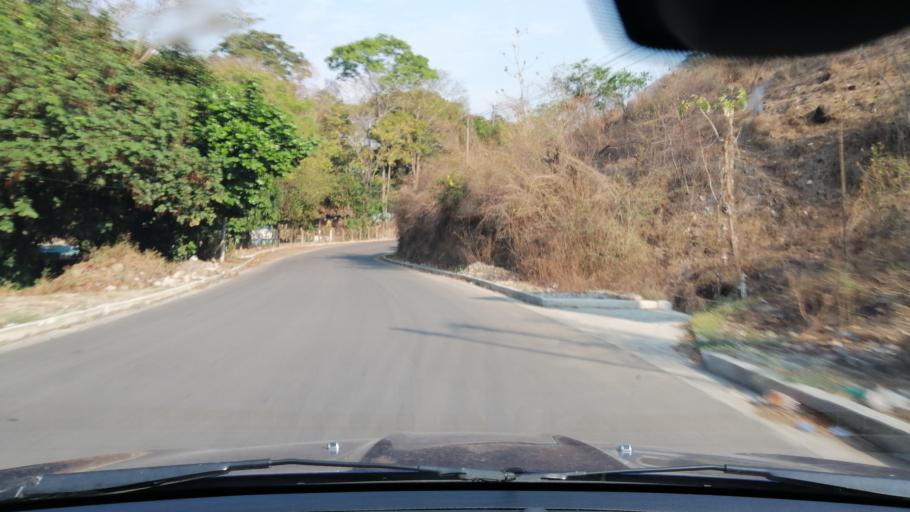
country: SV
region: Santa Ana
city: Texistepeque
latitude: 14.2248
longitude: -89.4549
